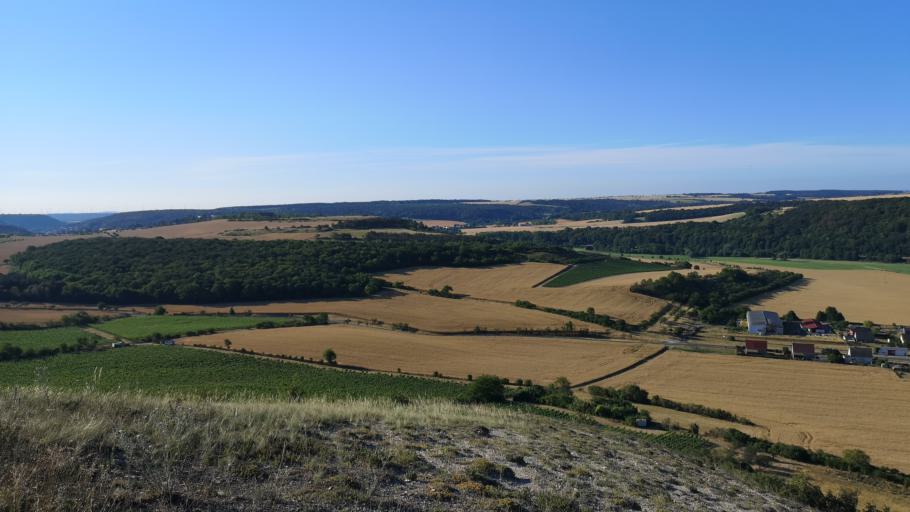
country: DE
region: Saxony-Anhalt
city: Laucha
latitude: 51.2267
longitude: 11.7072
